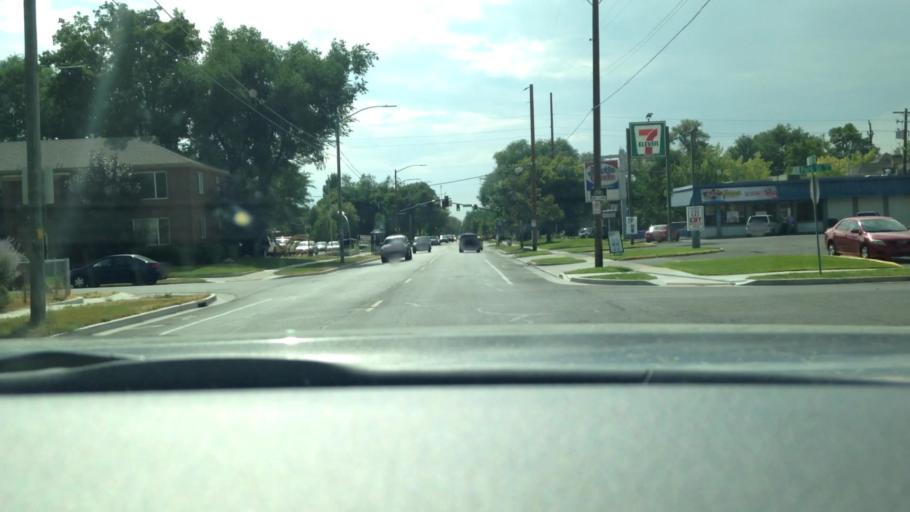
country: US
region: Utah
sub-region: Salt Lake County
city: South Salt Lake
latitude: 40.7335
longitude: -111.8750
